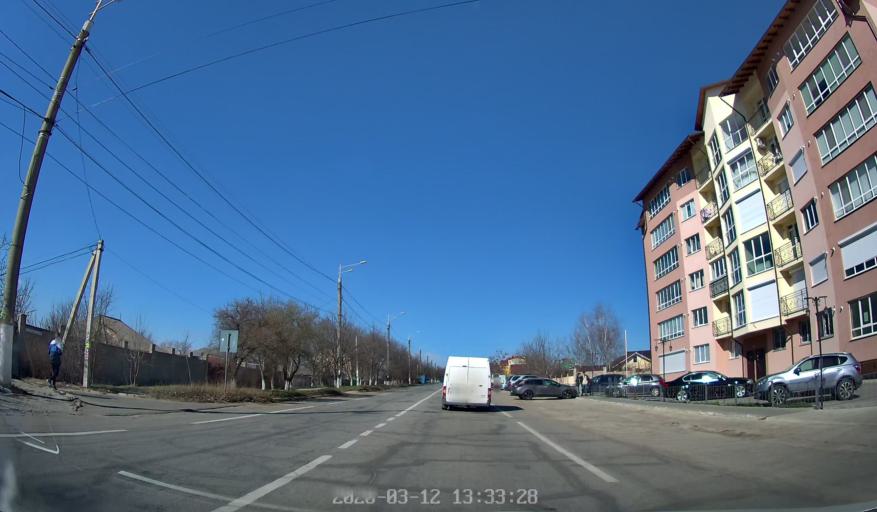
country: MD
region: Laloveni
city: Ialoveni
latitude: 46.9570
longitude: 28.7690
